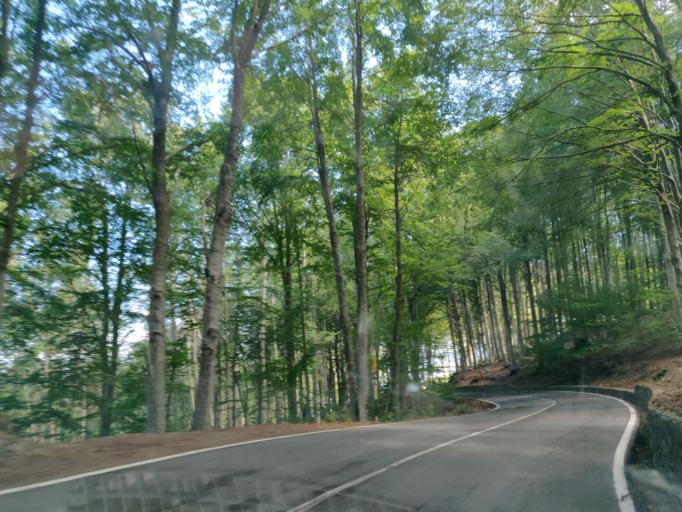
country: IT
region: Tuscany
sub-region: Provincia di Siena
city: Abbadia San Salvatore
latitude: 42.9008
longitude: 11.6421
